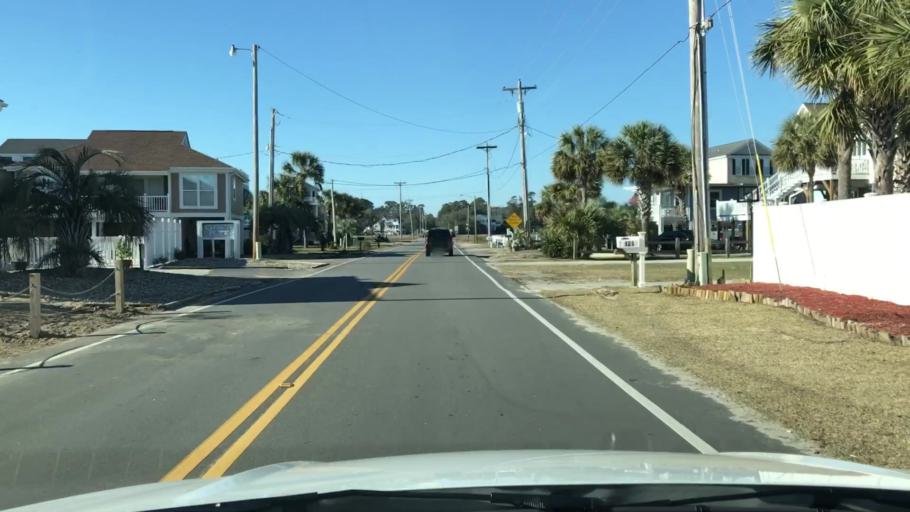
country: US
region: South Carolina
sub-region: Horry County
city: Garden City
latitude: 33.5812
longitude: -78.9954
